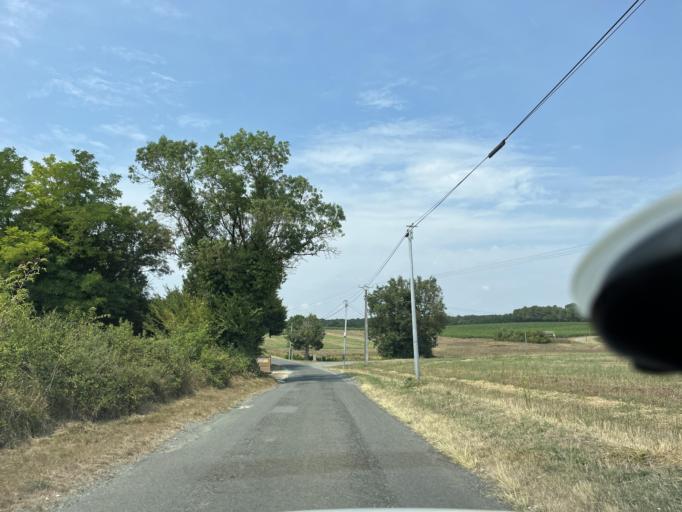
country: FR
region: Poitou-Charentes
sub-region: Departement de la Charente-Maritime
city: Pons
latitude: 45.5934
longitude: -0.5767
